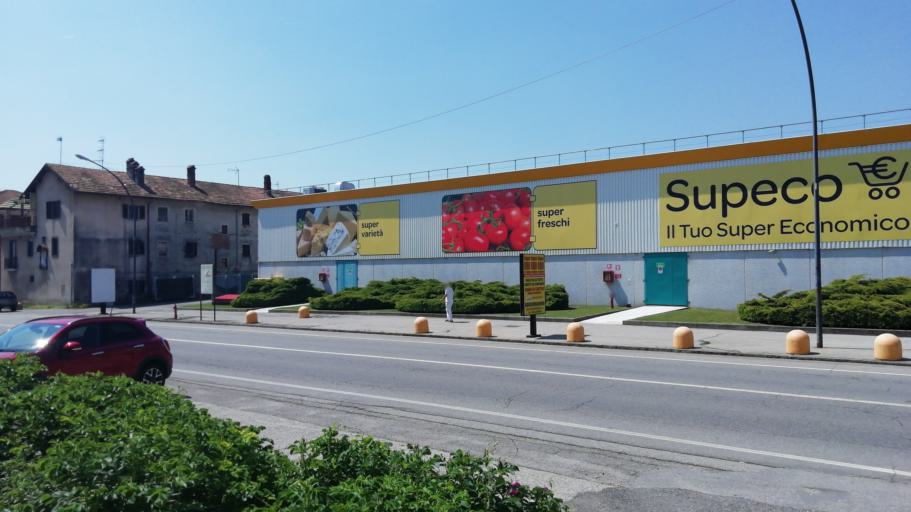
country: IT
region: Piedmont
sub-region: Provincia di Novara
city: Borgomanero
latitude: 45.7086
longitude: 8.4544
